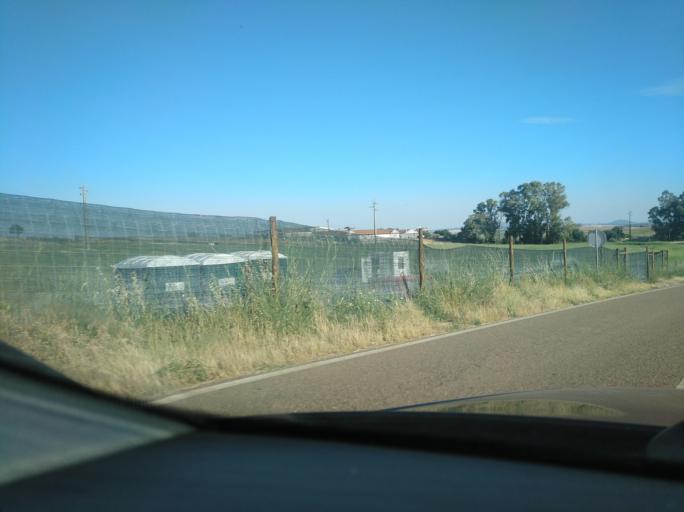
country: PT
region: Portalegre
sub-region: Elvas
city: Elvas
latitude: 38.8386
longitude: -7.1620
